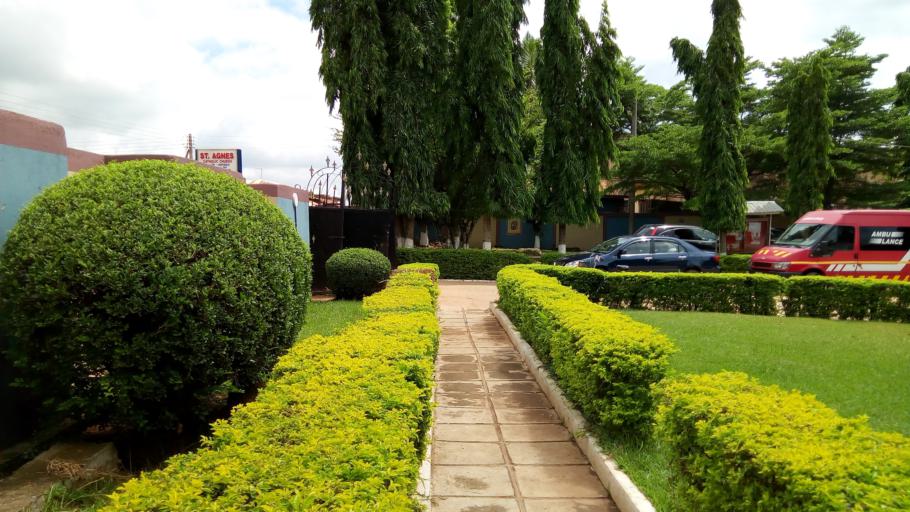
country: GH
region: Ashanti
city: Tafo
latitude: 6.9316
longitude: -1.6848
